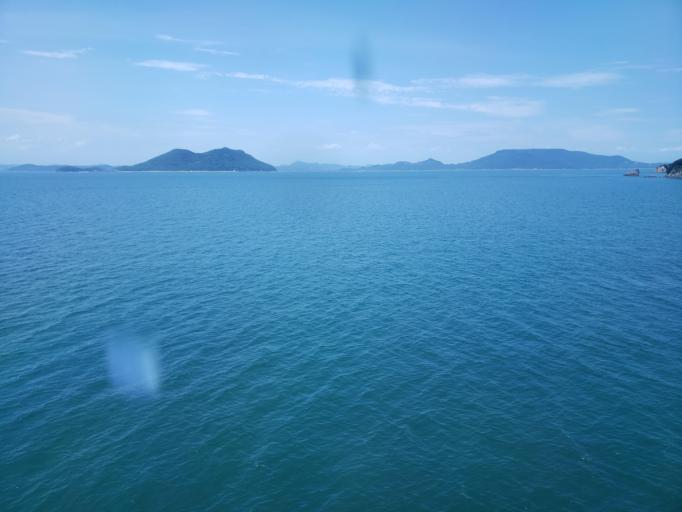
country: JP
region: Kagawa
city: Takamatsu-shi
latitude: 34.3933
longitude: 134.0980
